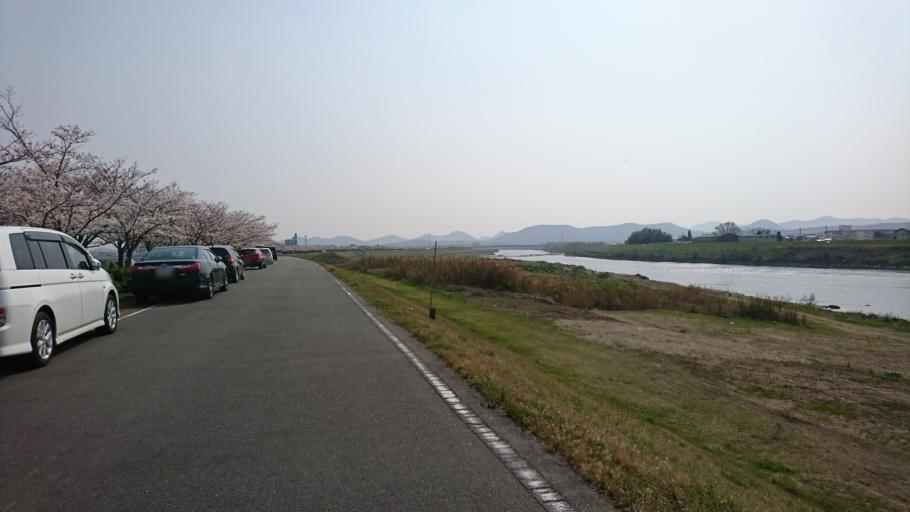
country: JP
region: Hyogo
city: Ono
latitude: 34.8731
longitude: 134.9262
